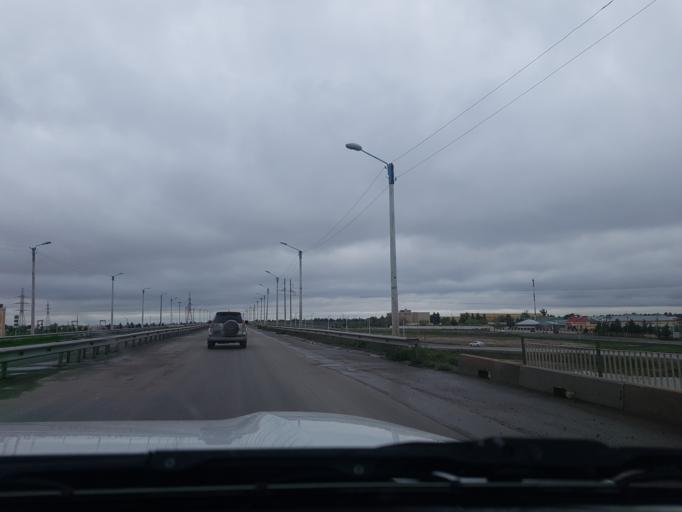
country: TM
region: Mary
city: Mary
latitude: 37.5917
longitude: 61.8846
